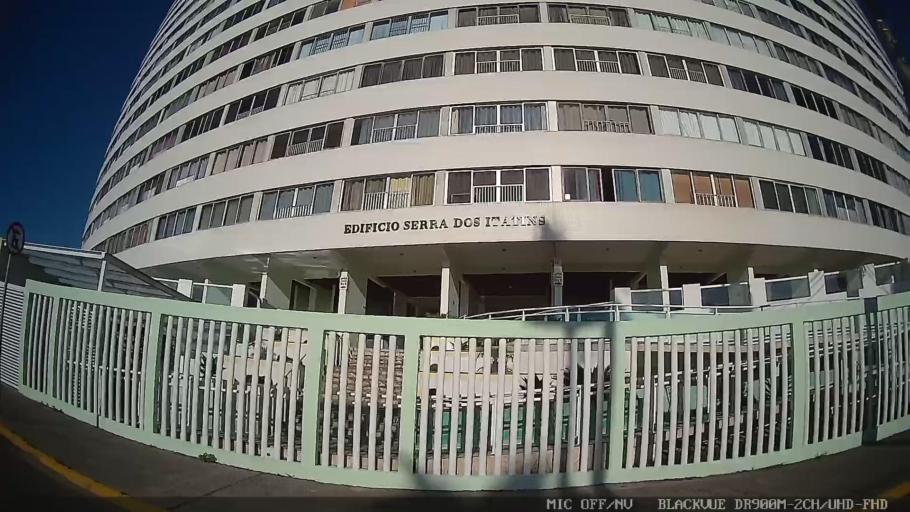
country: BR
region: Sao Paulo
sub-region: Peruibe
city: Peruibe
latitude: -24.3246
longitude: -46.9958
